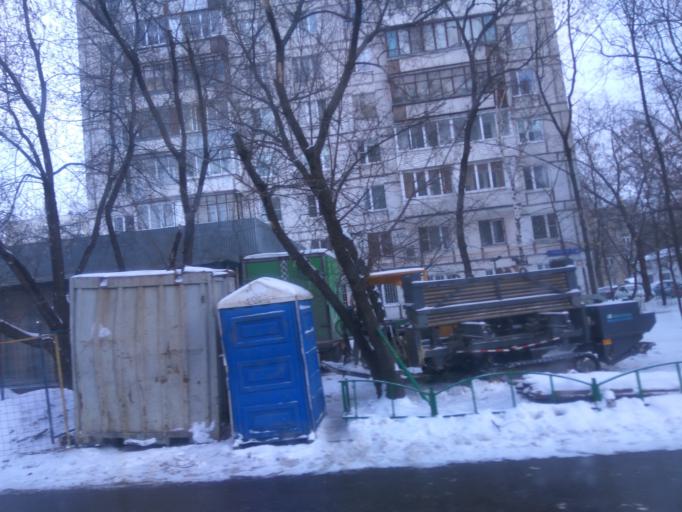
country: RU
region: Moscow
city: Mar'ina Roshcha
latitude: 55.8053
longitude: 37.5732
